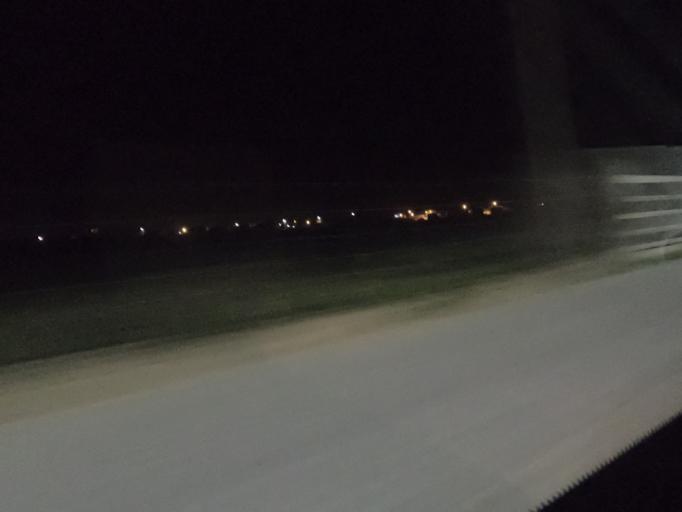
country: PT
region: Setubal
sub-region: Setubal
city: Setubal
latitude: 38.5180
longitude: -8.8252
